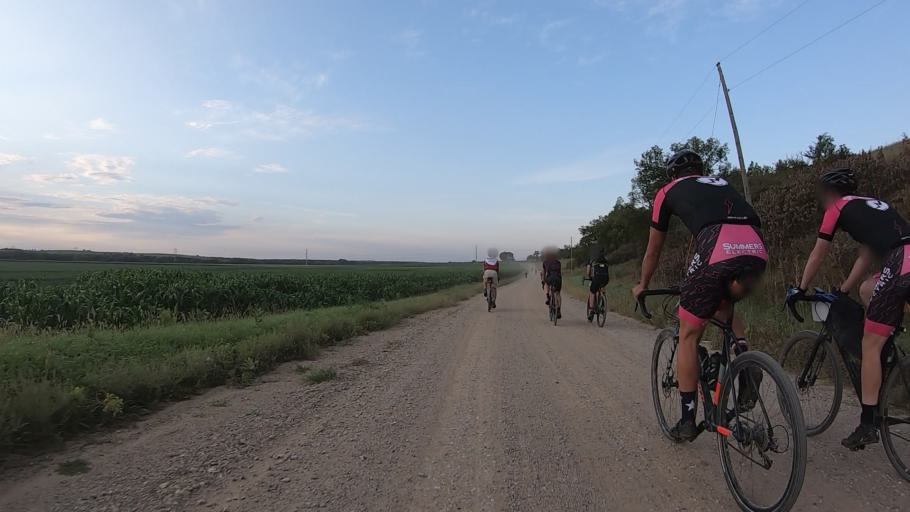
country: US
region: Kansas
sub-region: Marshall County
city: Marysville
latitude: 39.8257
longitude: -96.6656
